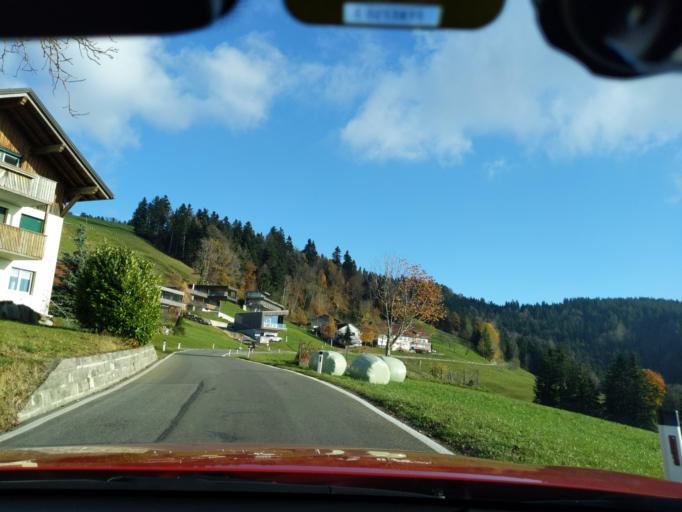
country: AT
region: Vorarlberg
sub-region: Politischer Bezirk Bregenz
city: Eichenberg
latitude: 47.5461
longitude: 9.7887
